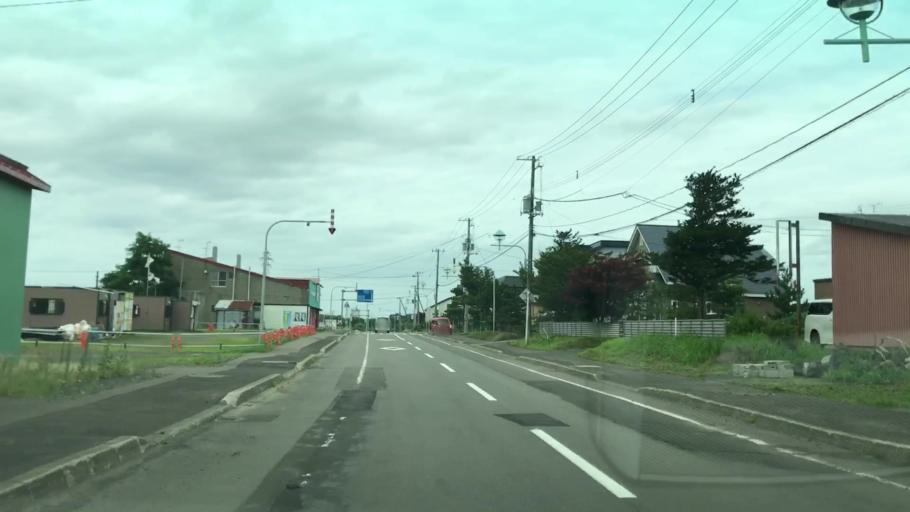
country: JP
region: Hokkaido
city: Iwanai
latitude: 42.9843
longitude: 140.6154
